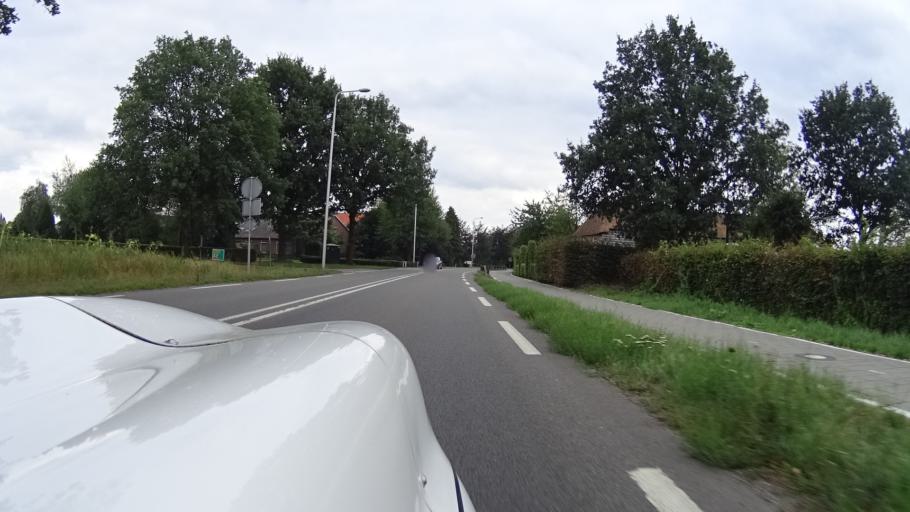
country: NL
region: North Brabant
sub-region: Gemeente Boekel
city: Boekel
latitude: 51.5823
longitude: 5.6891
